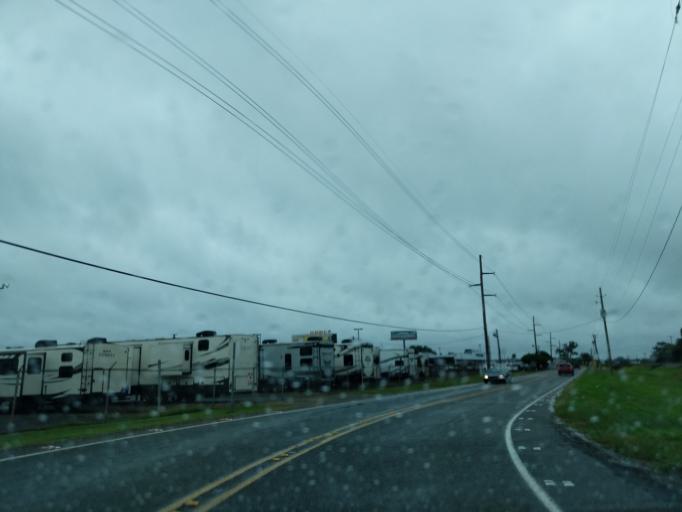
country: US
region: Louisiana
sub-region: Bossier Parish
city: Bossier City
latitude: 32.5259
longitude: -93.6795
